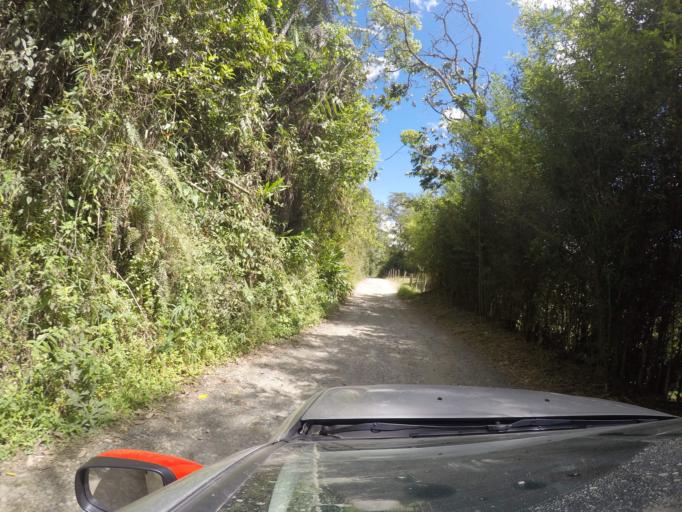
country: CO
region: Quindio
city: Salento
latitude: 4.6384
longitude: -75.5882
